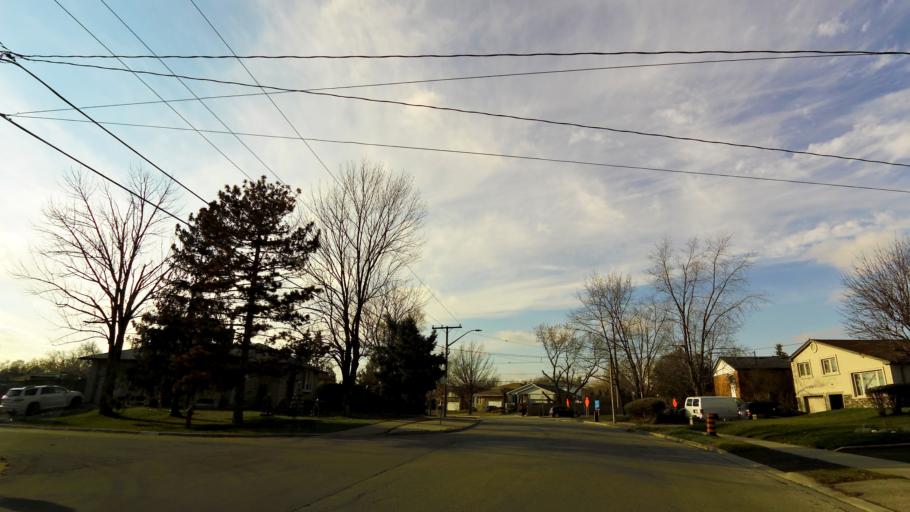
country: CA
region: Ontario
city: Mississauga
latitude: 43.5641
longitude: -79.6662
